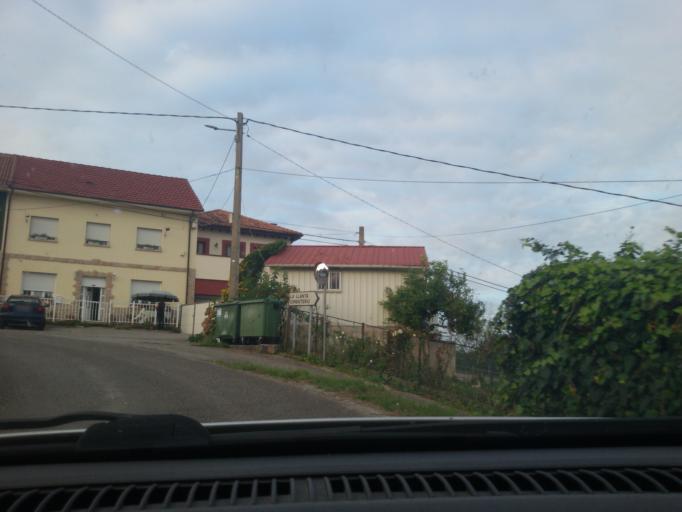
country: ES
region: Asturias
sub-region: Province of Asturias
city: Bimenes
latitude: 43.3388
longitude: -5.5837
